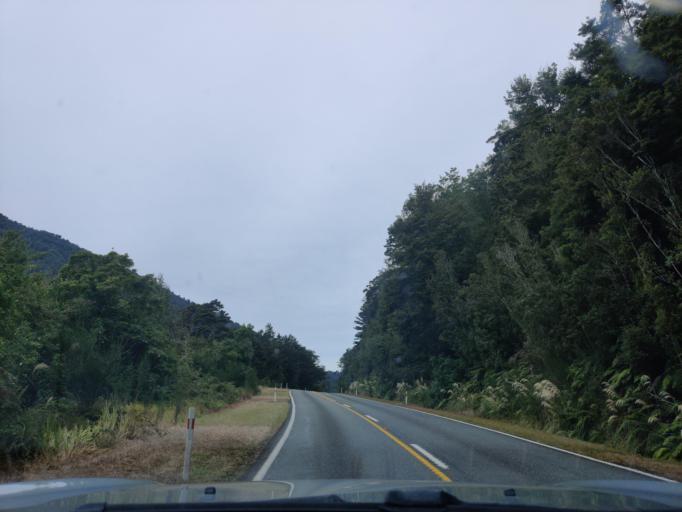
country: NZ
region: West Coast
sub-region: Buller District
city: Westport
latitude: -41.8539
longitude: 171.7500
